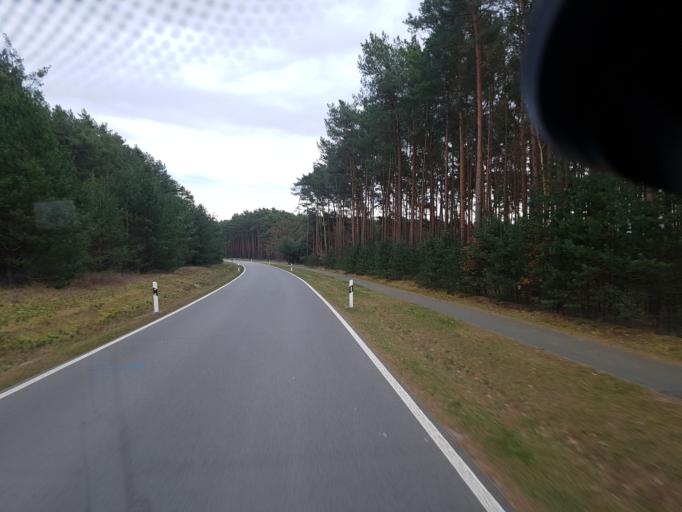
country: DE
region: Brandenburg
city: Mixdorf
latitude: 52.1987
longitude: 14.3806
